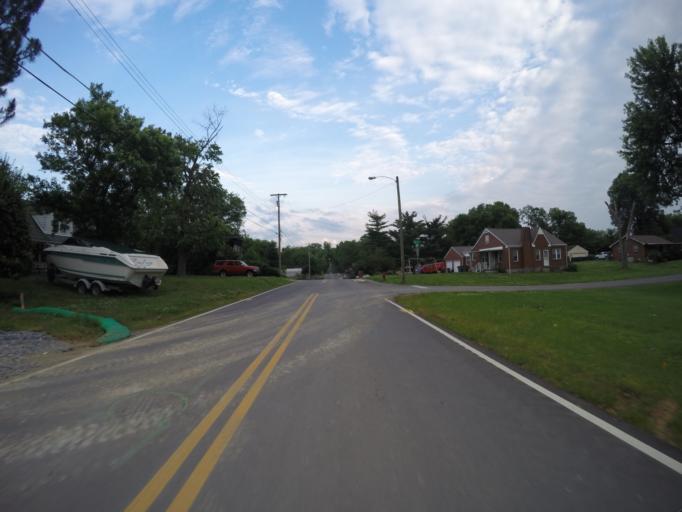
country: US
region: Tennessee
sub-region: Davidson County
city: Lakewood
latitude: 36.2492
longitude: -86.6379
